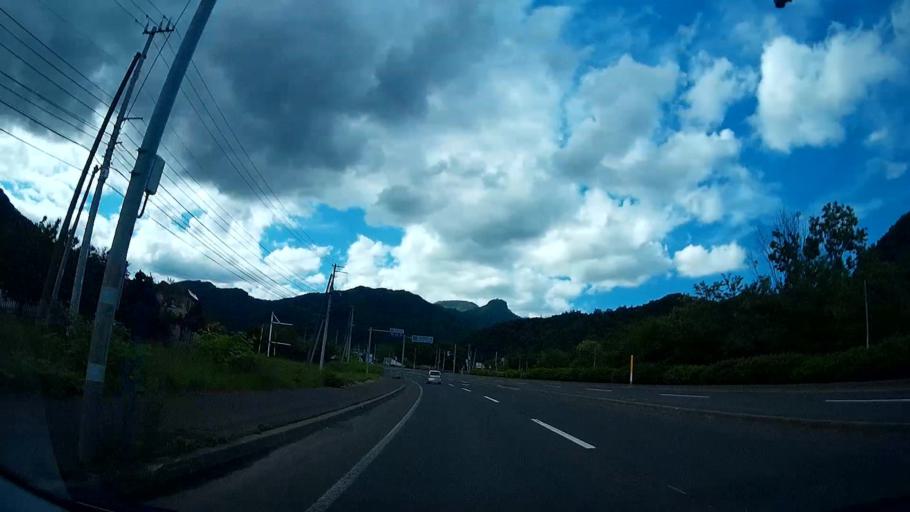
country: JP
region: Hokkaido
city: Sapporo
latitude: 42.9642
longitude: 141.2208
